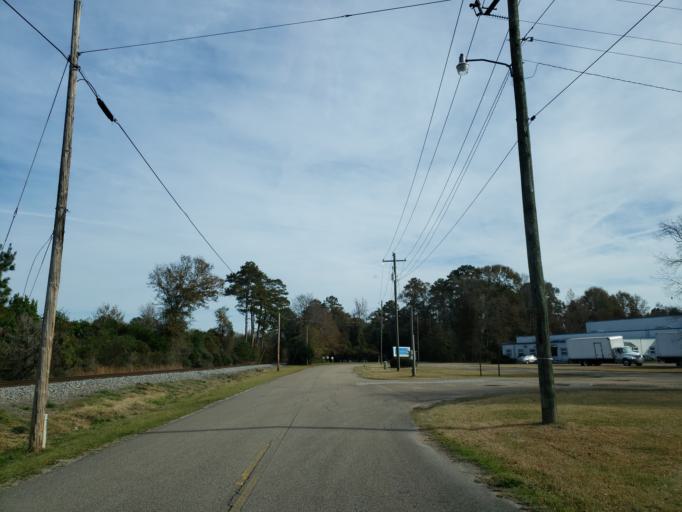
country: US
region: Mississippi
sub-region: Forrest County
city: Glendale
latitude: 31.3505
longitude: -89.3218
